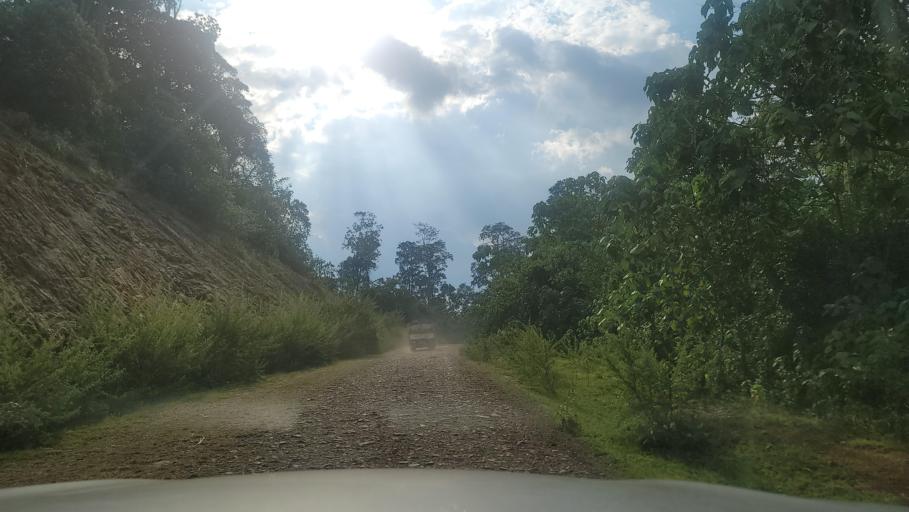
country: ET
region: Southern Nations, Nationalities, and People's Region
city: Bonga
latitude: 7.5768
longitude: 36.1631
